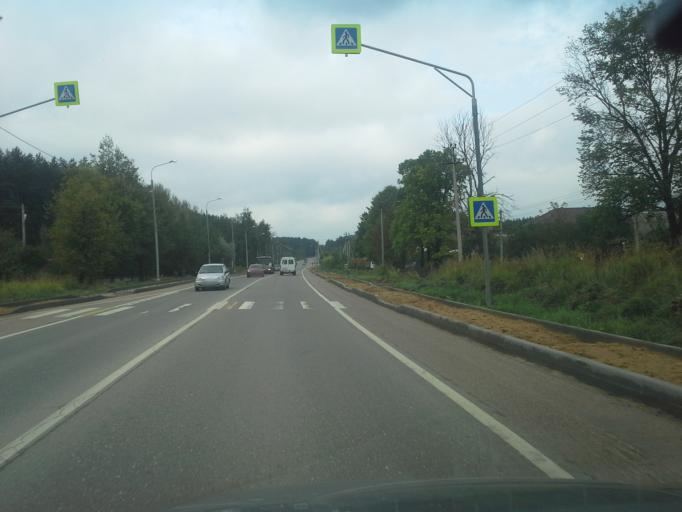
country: RU
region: Moskovskaya
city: Kubinka
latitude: 55.5721
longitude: 36.6861
